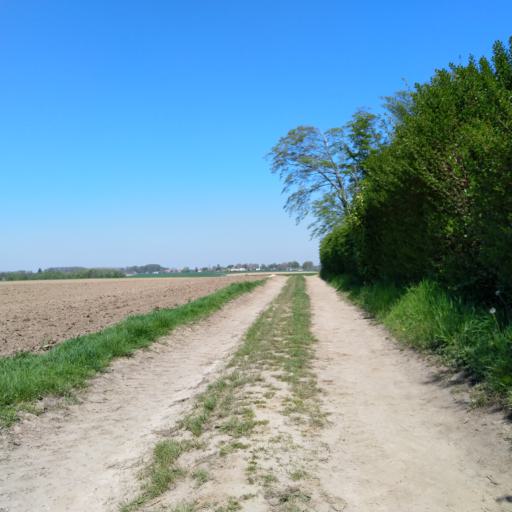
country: BE
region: Wallonia
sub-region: Province du Hainaut
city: Jurbise
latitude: 50.5351
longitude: 3.9037
